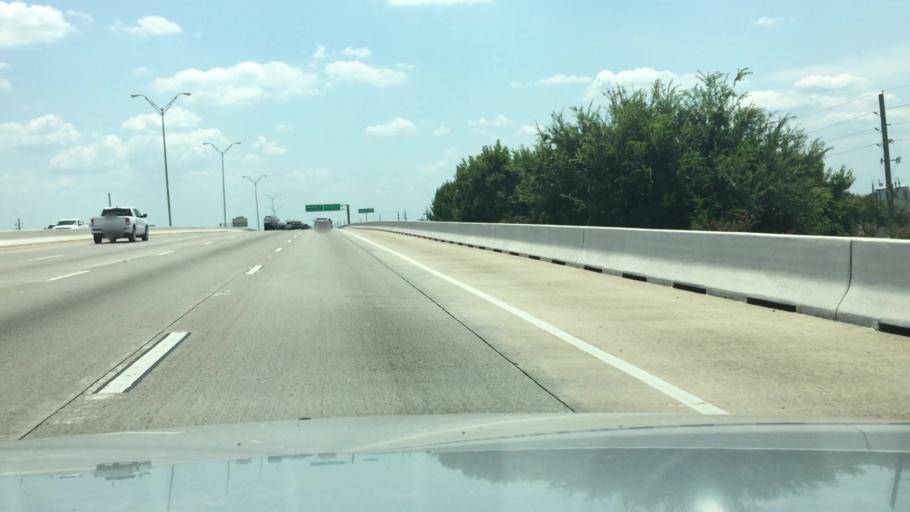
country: US
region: Texas
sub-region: Fort Bend County
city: Meadows Place
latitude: 29.7069
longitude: -95.5579
